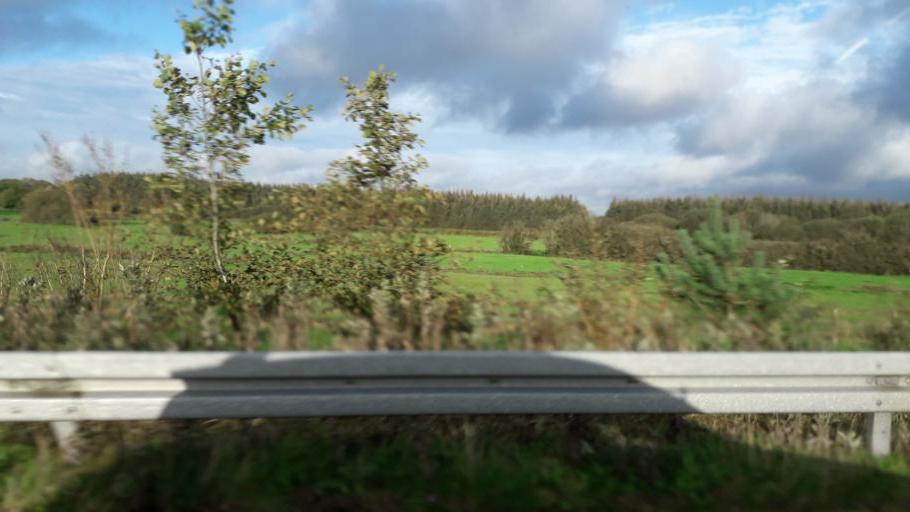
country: IE
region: Connaught
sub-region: Roscommon
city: Ballaghaderreen
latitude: 53.9091
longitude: -8.5490
